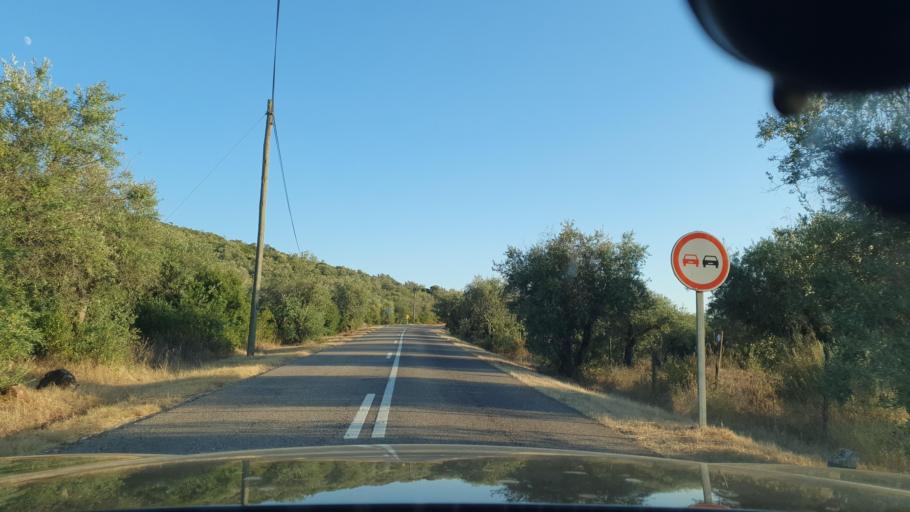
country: PT
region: Evora
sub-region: Estremoz
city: Estremoz
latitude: 38.9261
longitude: -7.6654
